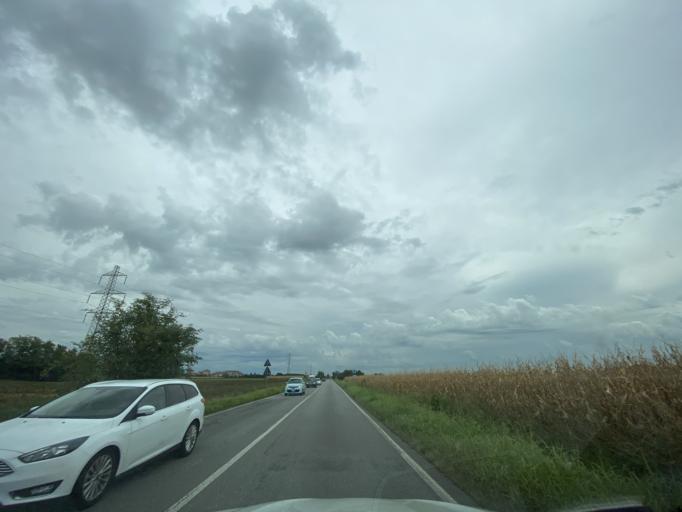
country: IT
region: Lombardy
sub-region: Provincia di Monza e Brianza
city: Caponago
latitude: 45.5597
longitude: 9.3649
